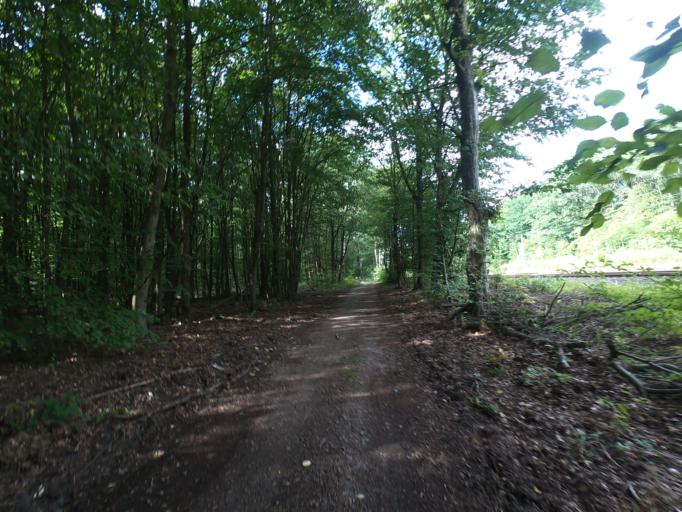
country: DE
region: Hesse
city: Langen
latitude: 50.0127
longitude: 8.6594
